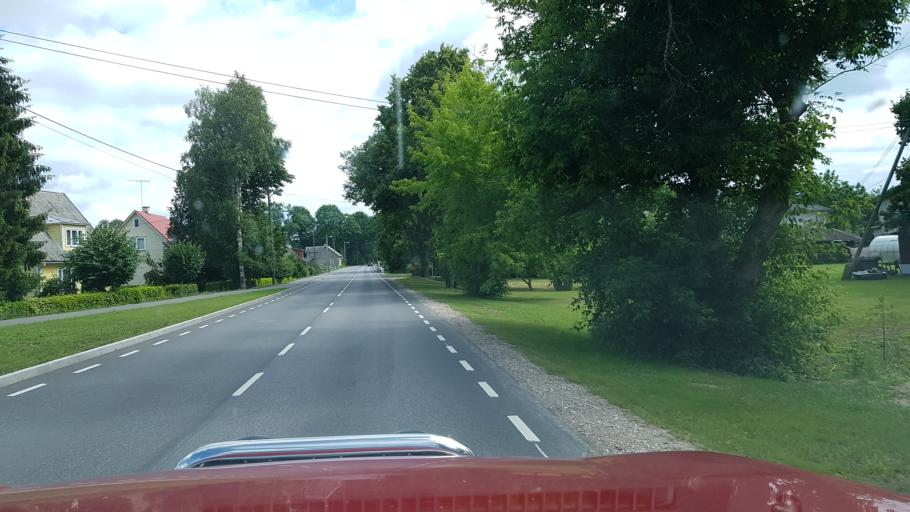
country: EE
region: Jogevamaa
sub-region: Mustvee linn
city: Mustvee
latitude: 58.8481
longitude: 26.9223
